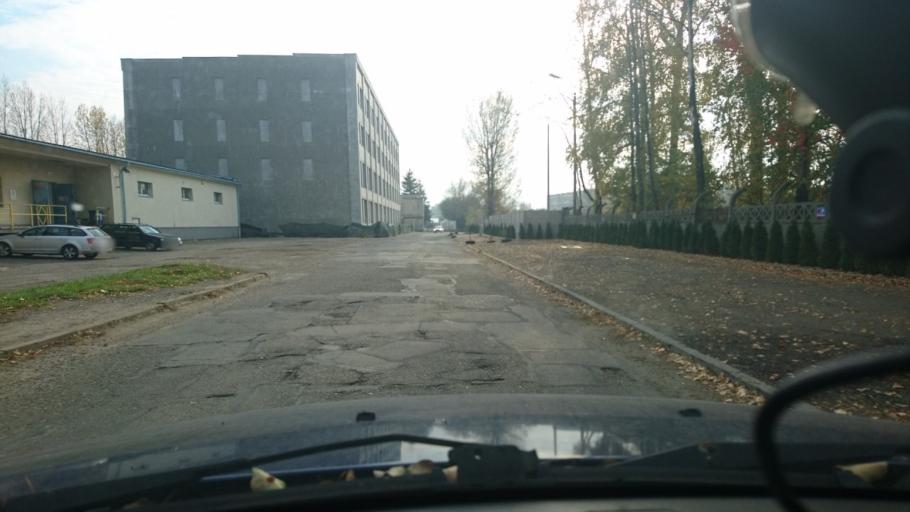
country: PL
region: Silesian Voivodeship
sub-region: Bielsko-Biala
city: Bielsko-Biala
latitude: 49.8318
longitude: 19.0614
